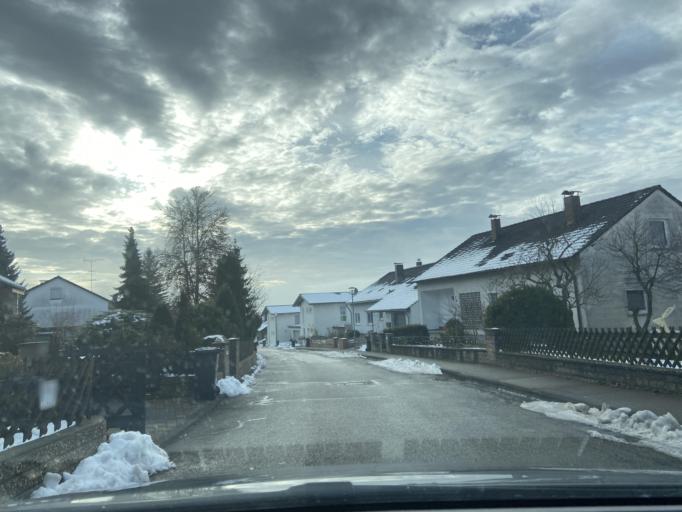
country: DE
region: Baden-Wuerttemberg
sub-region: Tuebingen Region
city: Gammertingen
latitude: 48.2526
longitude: 9.2233
